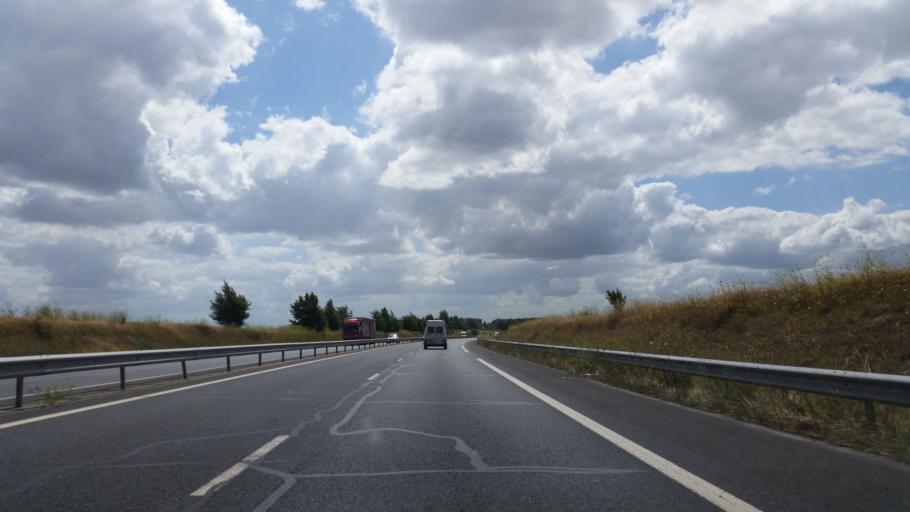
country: FR
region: Lower Normandy
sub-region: Departement du Calvados
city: Falaise
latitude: 48.9192
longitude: -0.2058
